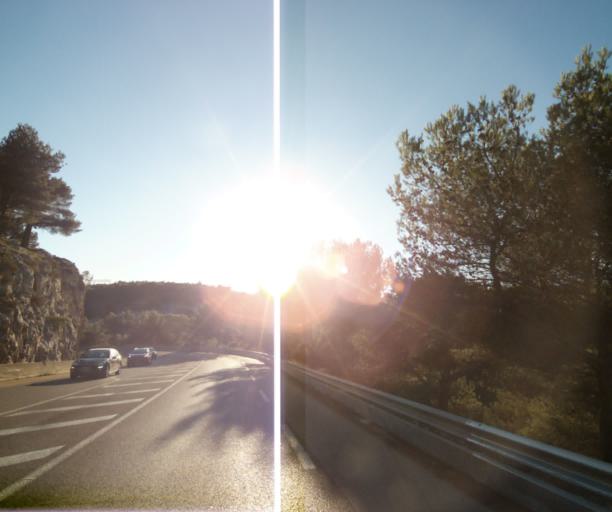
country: FR
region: Provence-Alpes-Cote d'Azur
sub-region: Departement des Bouches-du-Rhone
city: Carnoux-en-Provence
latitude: 43.2419
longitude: 5.5434
